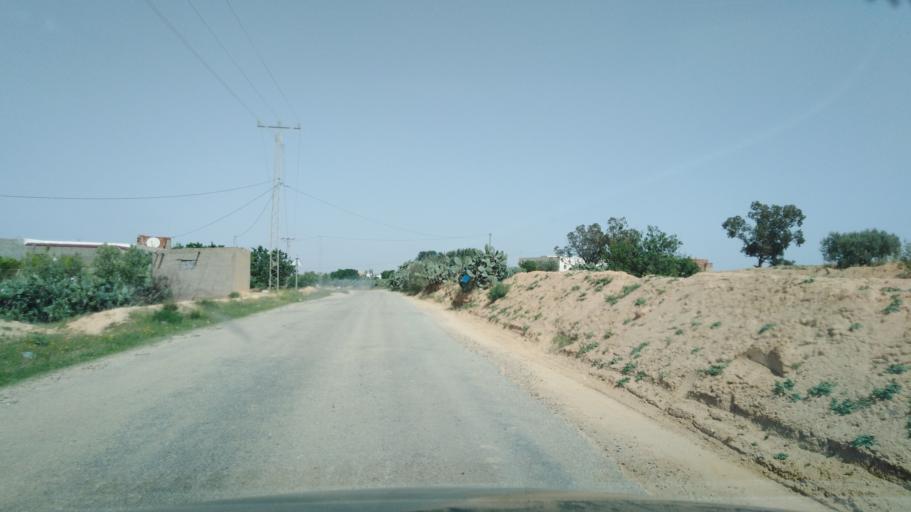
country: TN
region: Safaqis
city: Sfax
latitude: 34.7184
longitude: 10.5319
